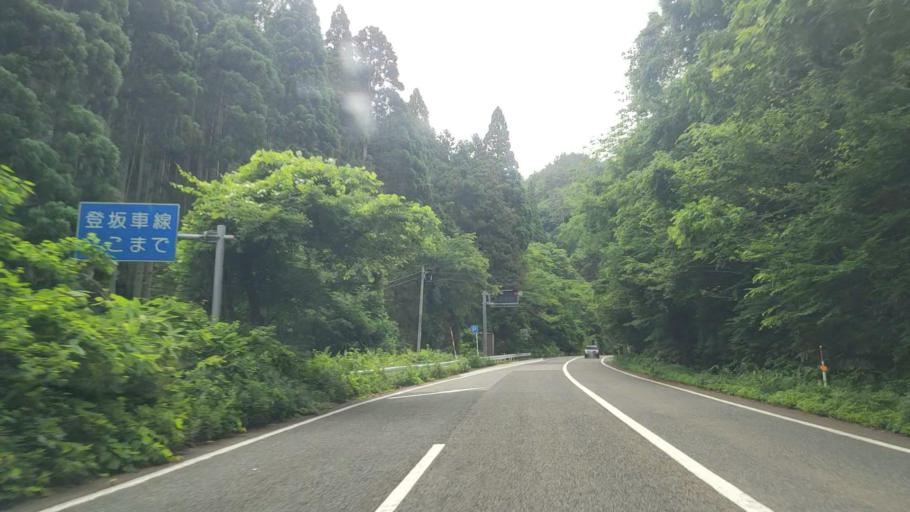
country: JP
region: Tottori
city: Yonago
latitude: 35.2712
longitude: 133.4338
